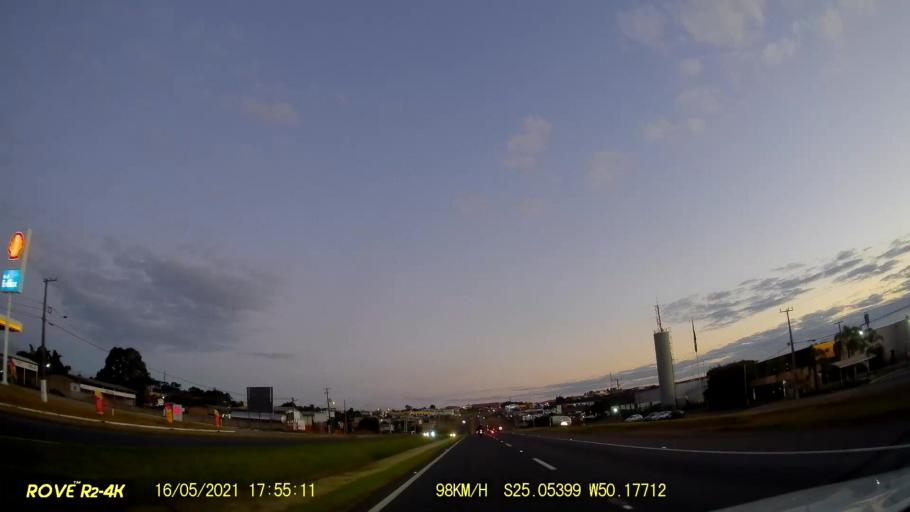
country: BR
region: Parana
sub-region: Ponta Grossa
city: Ponta Grossa
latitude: -25.0541
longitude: -50.1771
